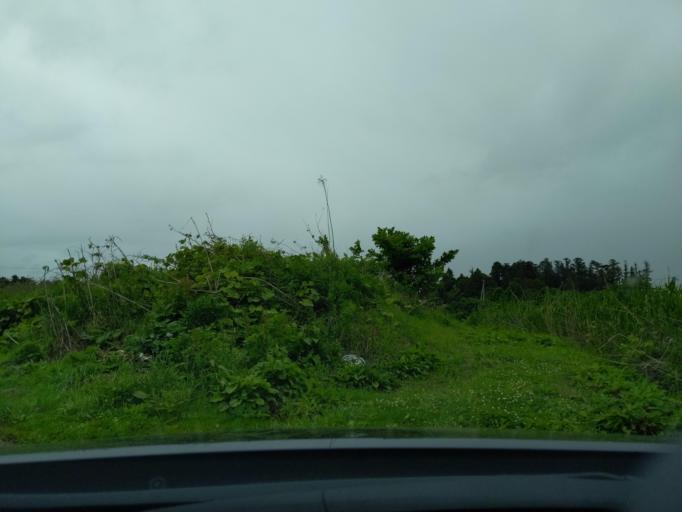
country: JP
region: Fukushima
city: Koriyama
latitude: 37.3689
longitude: 140.3170
